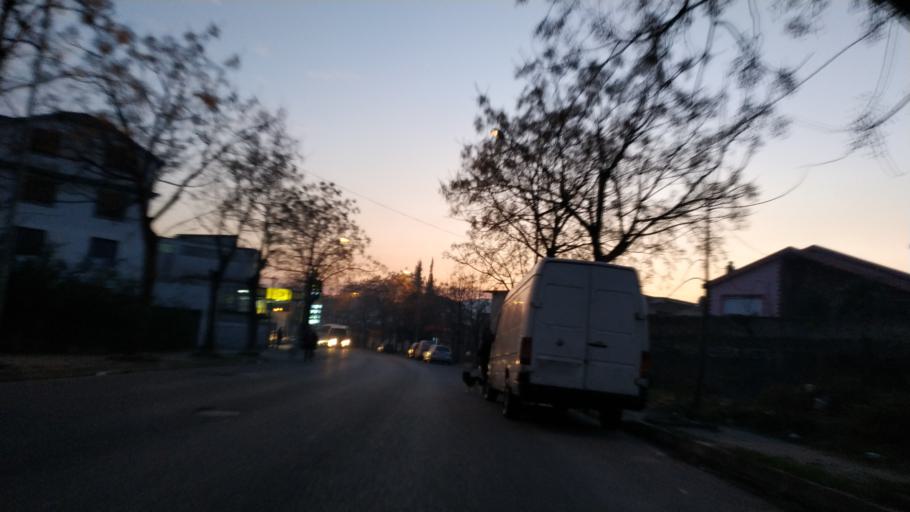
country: AL
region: Shkoder
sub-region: Rrethi i Shkodres
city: Shkoder
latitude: 42.0773
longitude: 19.5042
